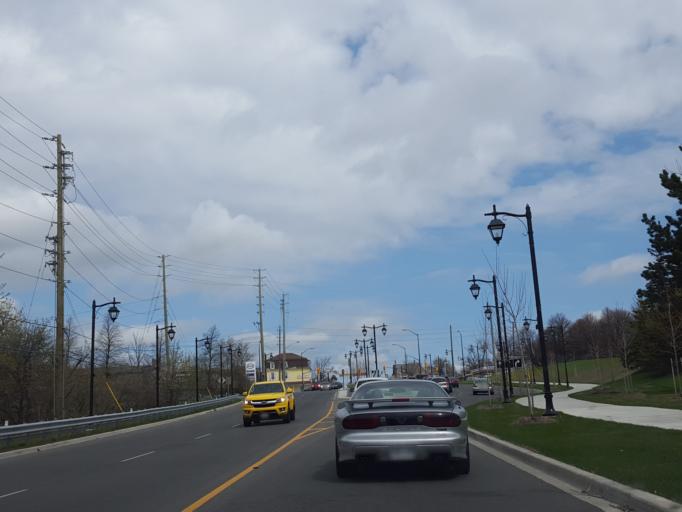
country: CA
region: Ontario
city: Markham
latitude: 43.8719
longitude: -79.2593
